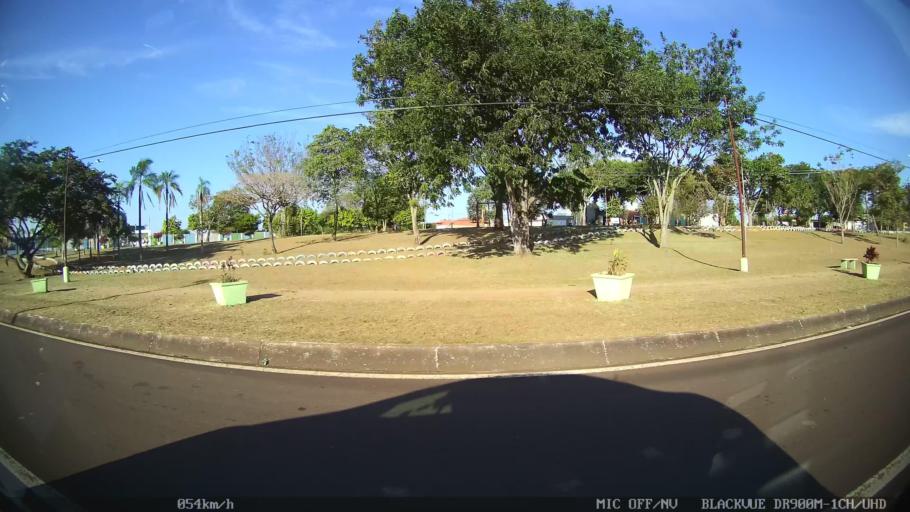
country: BR
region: Sao Paulo
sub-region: Franca
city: Franca
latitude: -20.5074
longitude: -47.3722
